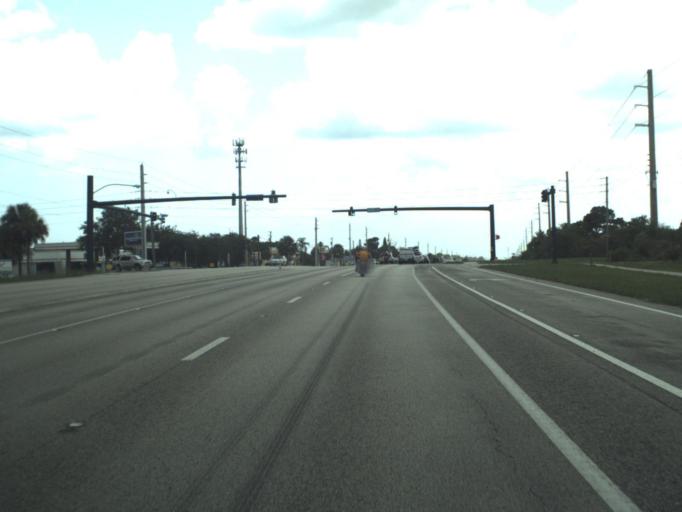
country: US
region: Florida
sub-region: Martin County
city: Hobe Sound
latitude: 27.0995
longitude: -80.1600
